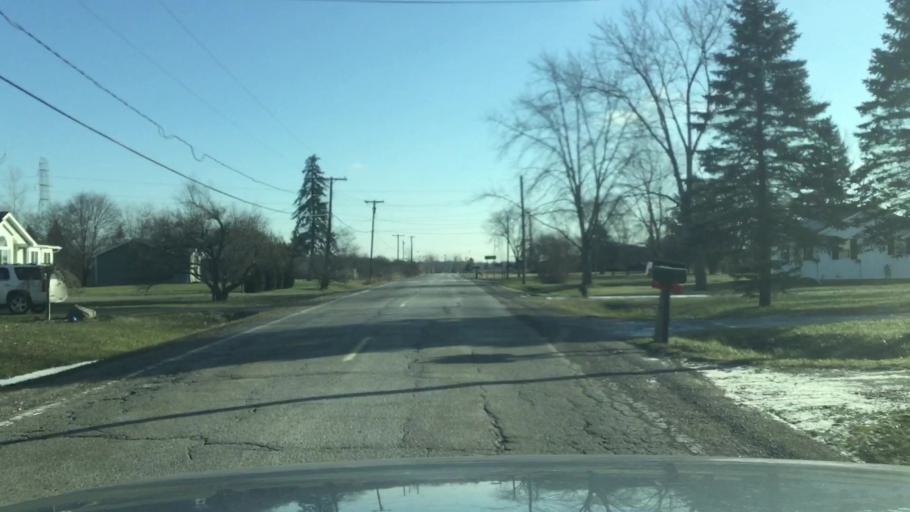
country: US
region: Michigan
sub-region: Genesee County
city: Grand Blanc
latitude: 42.9355
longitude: -83.6554
